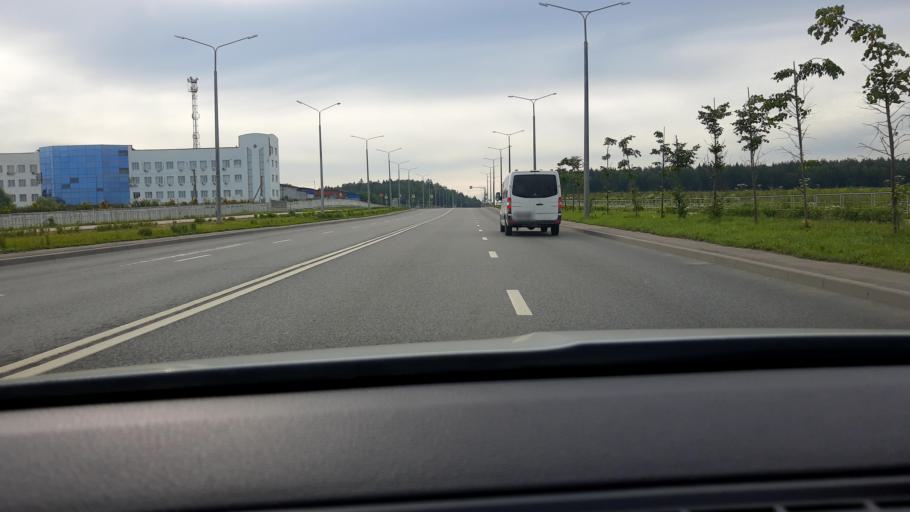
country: RU
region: Moskovskaya
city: Troitsk
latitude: 55.5084
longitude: 37.2520
